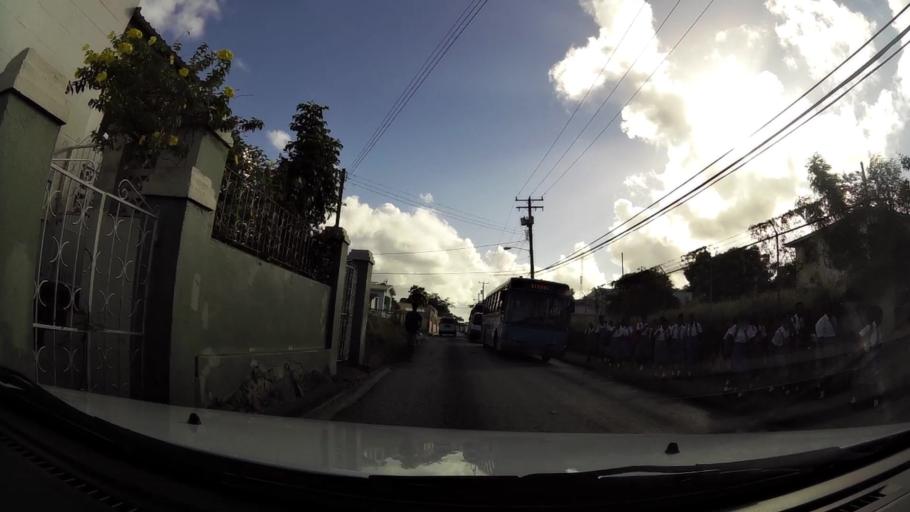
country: BB
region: Saint Michael
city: Bridgetown
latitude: 13.1025
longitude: -59.5965
